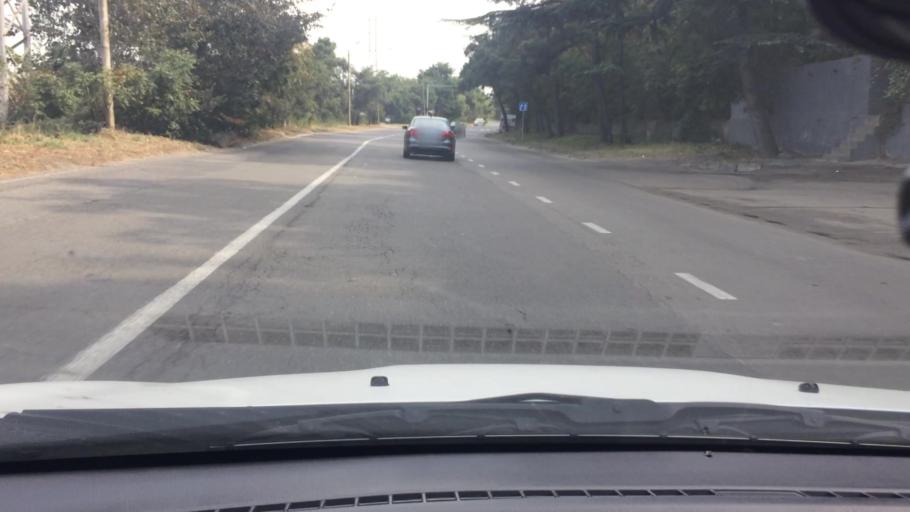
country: GE
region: T'bilisi
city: Tbilisi
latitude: 41.6700
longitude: 44.8522
